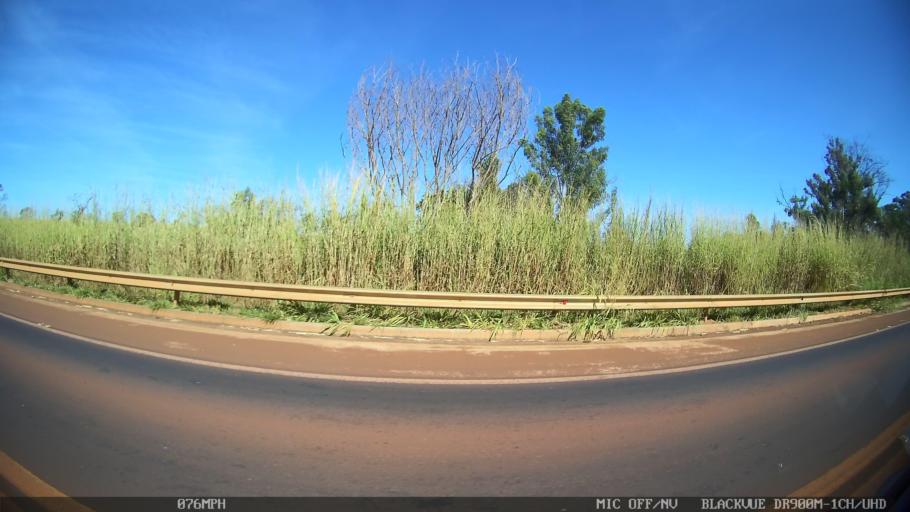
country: BR
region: Sao Paulo
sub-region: Sao Joaquim Da Barra
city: Sao Joaquim da Barra
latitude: -20.5471
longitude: -47.7678
